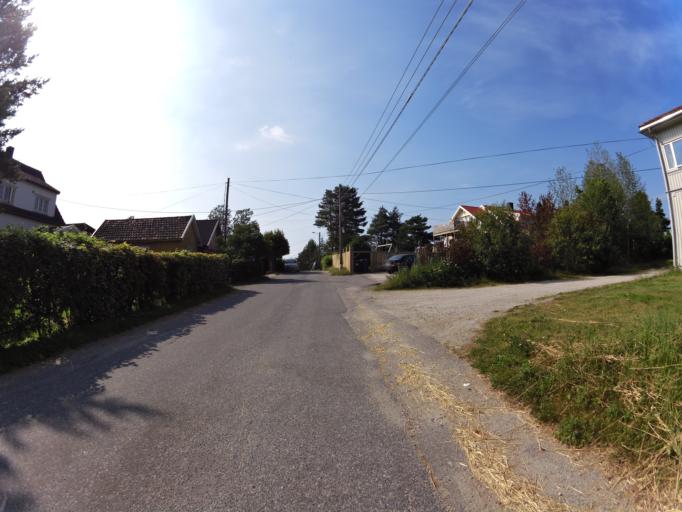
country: NO
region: Ostfold
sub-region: Fredrikstad
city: Fredrikstad
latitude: 59.2445
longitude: 10.9918
